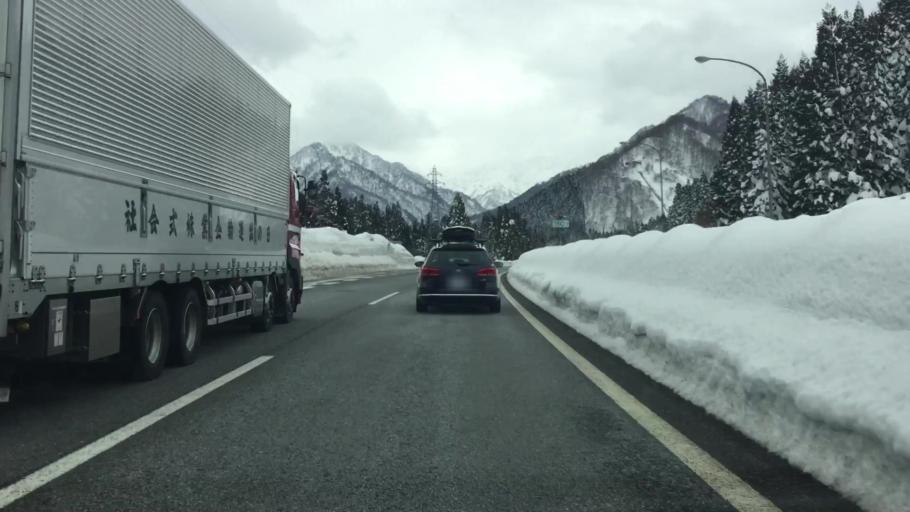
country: JP
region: Niigata
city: Shiozawa
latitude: 36.8856
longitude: 138.8509
